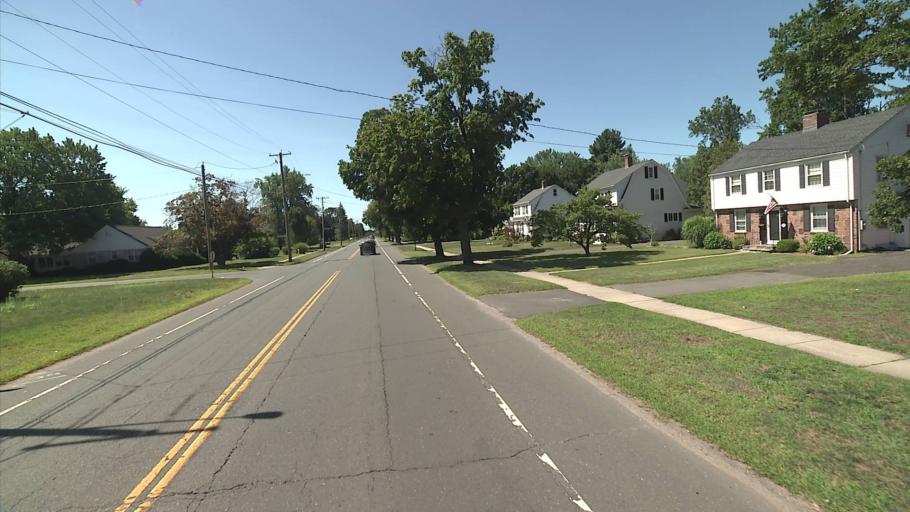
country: US
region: Connecticut
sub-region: Hartford County
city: Plainville
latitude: 41.6806
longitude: -72.8555
